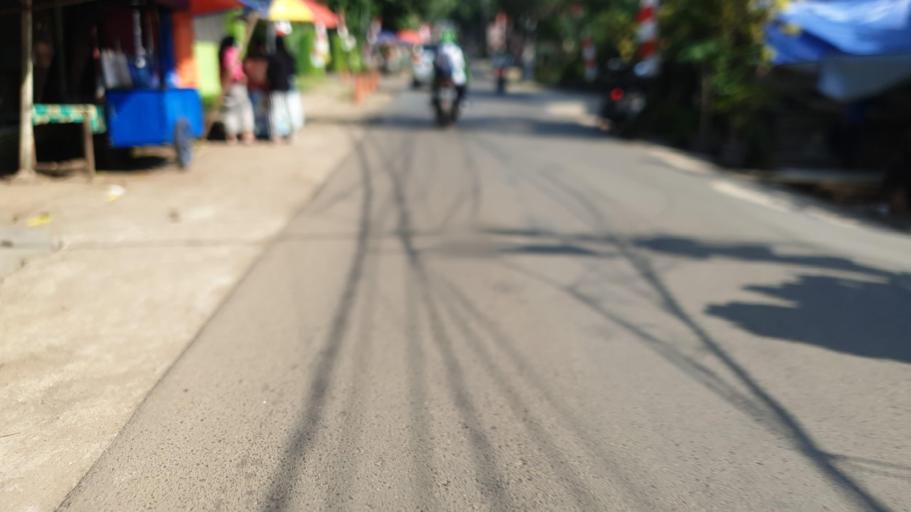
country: ID
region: Jakarta Raya
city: Jakarta
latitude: -6.2913
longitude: 106.8366
